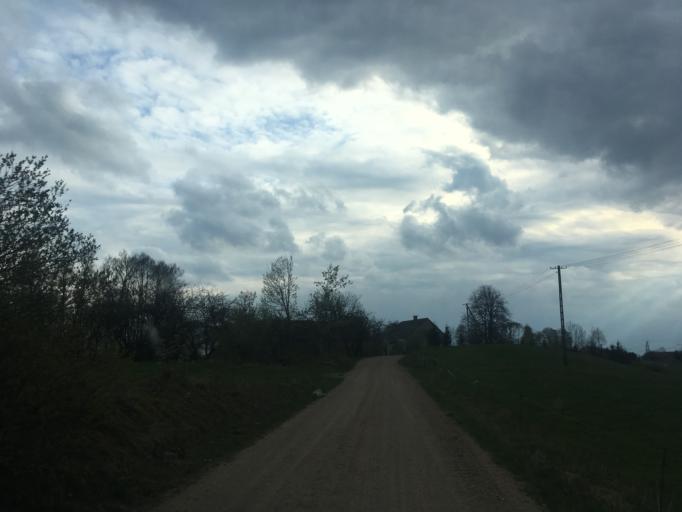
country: PL
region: Podlasie
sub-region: Powiat sejnenski
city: Punsk
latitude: 54.2865
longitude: 23.0986
